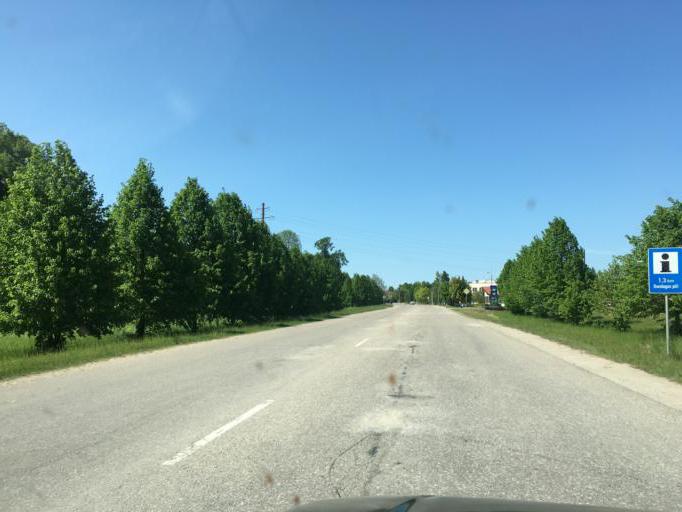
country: LV
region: Dundaga
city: Dundaga
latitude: 57.5018
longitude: 22.3523
